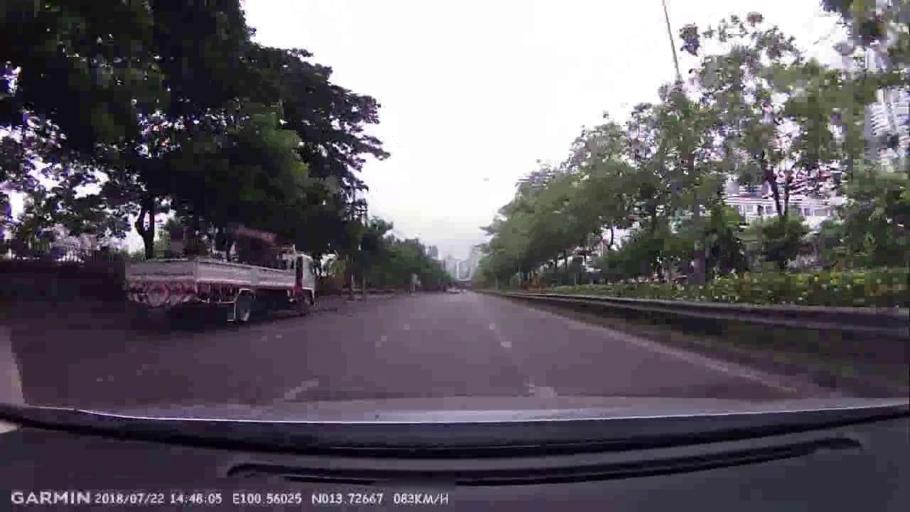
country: TH
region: Bangkok
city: Khlong Toei
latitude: 13.7268
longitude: 100.5602
